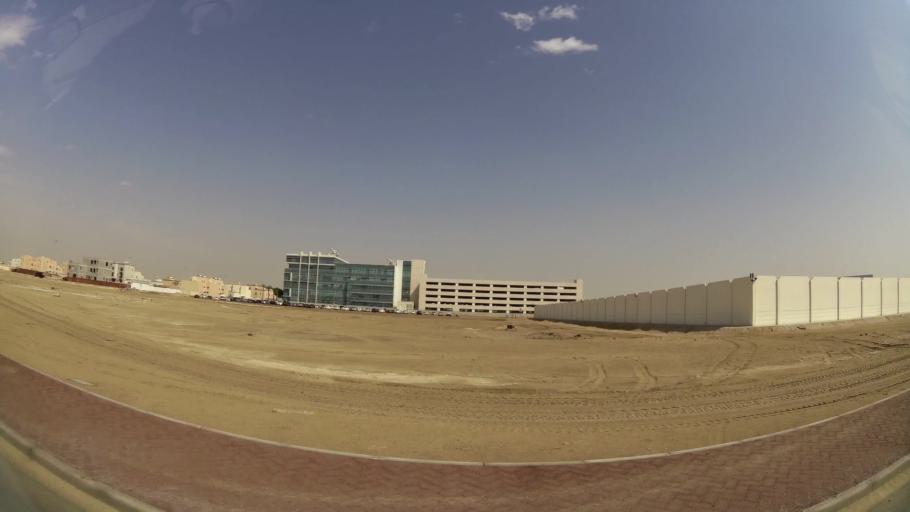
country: AE
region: Abu Dhabi
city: Abu Dhabi
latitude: 24.3162
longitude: 54.5514
